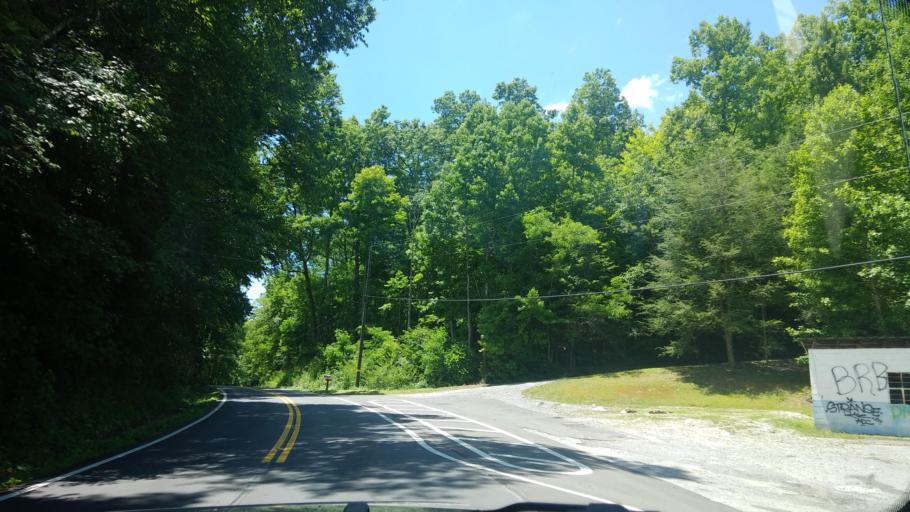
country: US
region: Tennessee
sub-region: Cocke County
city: Newport
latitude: 35.7851
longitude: -83.1978
